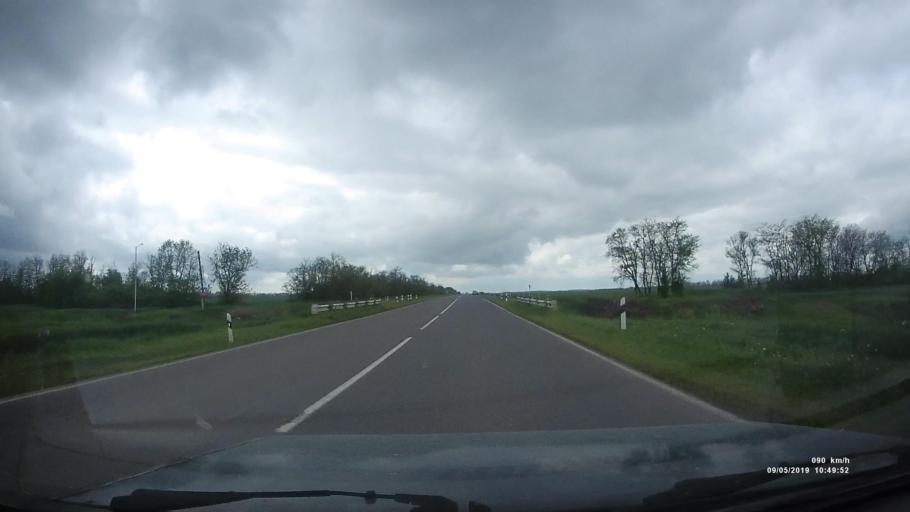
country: RU
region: Rostov
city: Peshkovo
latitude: 46.9365
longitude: 39.3554
